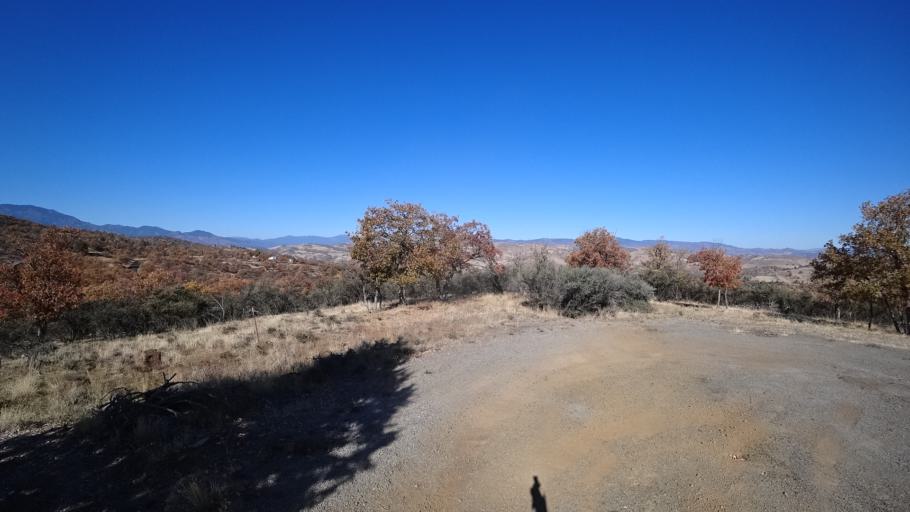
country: US
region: California
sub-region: Siskiyou County
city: Montague
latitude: 41.8770
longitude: -122.4853
